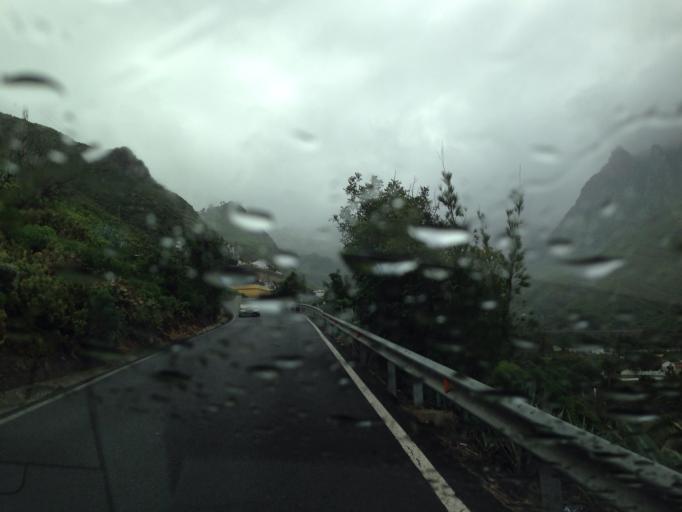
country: ES
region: Canary Islands
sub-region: Provincia de Las Palmas
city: Agaete
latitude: 28.0935
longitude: -15.6824
